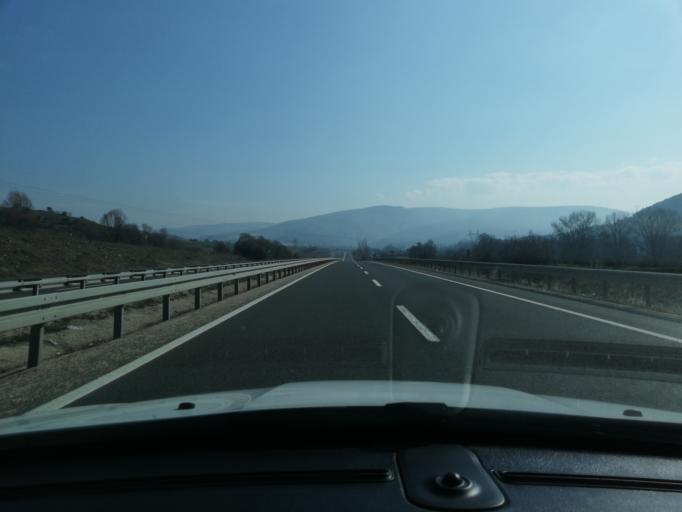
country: TR
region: Cankiri
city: Cerkes
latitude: 40.8362
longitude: 32.7444
